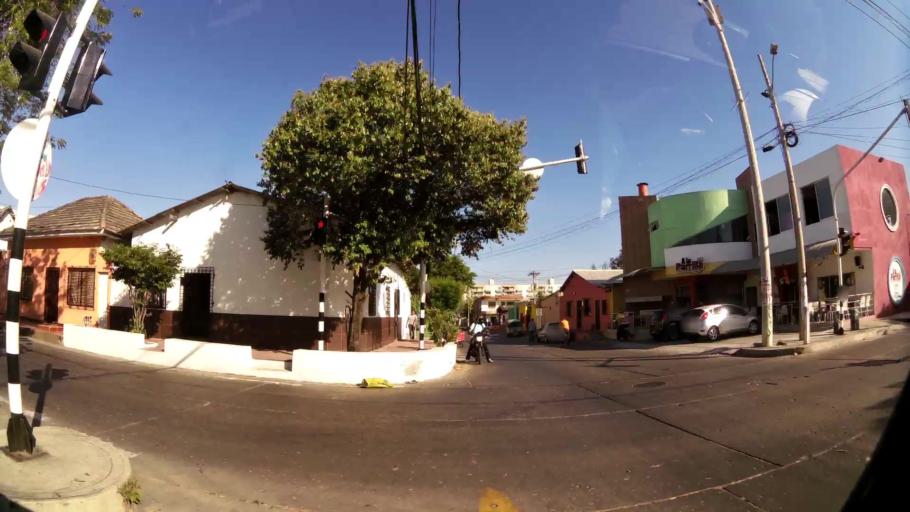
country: CO
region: Atlantico
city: Barranquilla
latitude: 10.9712
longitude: -74.7939
